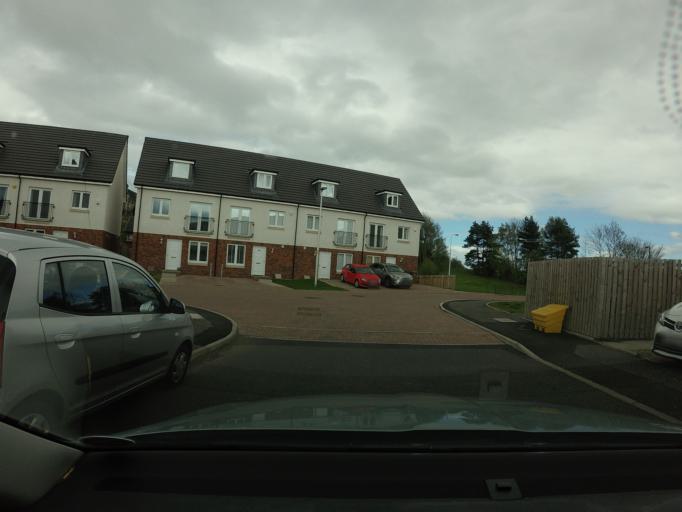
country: GB
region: Scotland
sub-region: Edinburgh
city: Kirkliston
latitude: 55.9534
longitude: -3.4052
